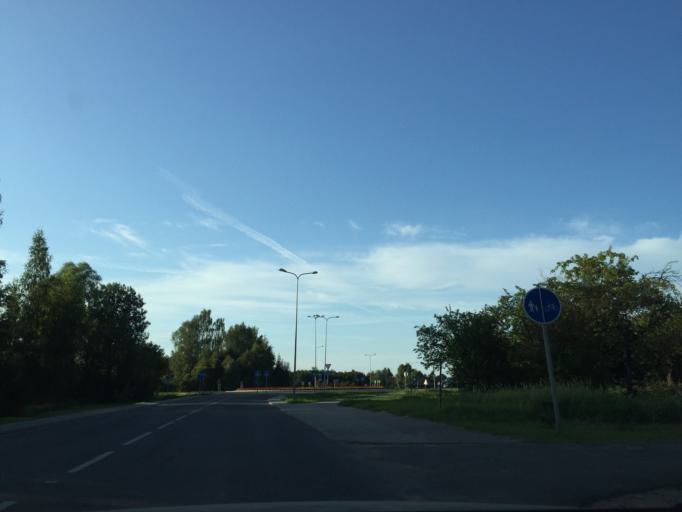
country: LT
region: Panevezys
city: Rokiskis
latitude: 55.9511
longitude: 25.5750
